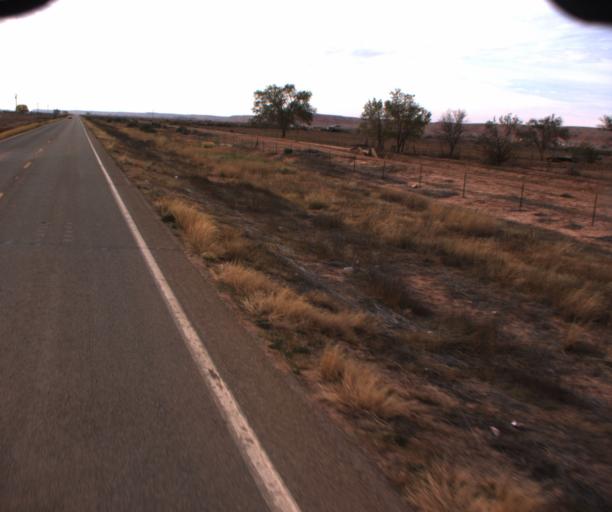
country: US
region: Arizona
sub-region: Apache County
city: Many Farms
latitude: 36.4178
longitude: -109.6067
